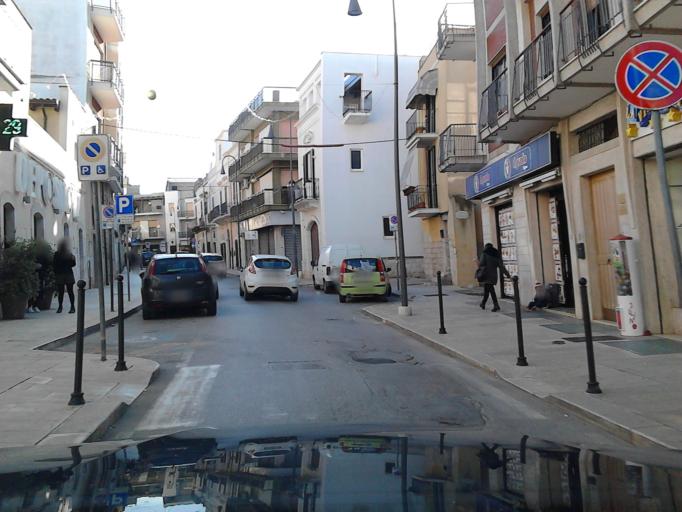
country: IT
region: Apulia
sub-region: Provincia di Bari
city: Rutigliano
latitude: 41.0103
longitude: 17.0034
